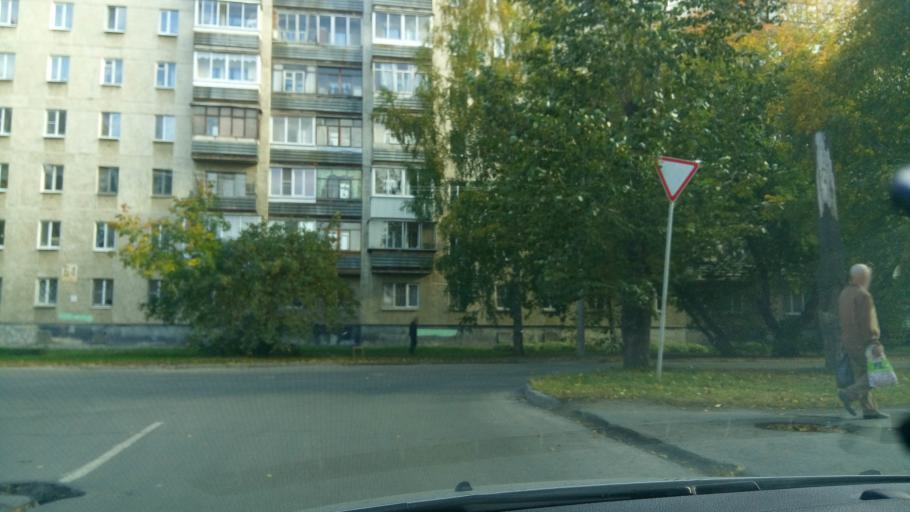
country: RU
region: Sverdlovsk
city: Yekaterinburg
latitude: 56.9047
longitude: 60.6051
